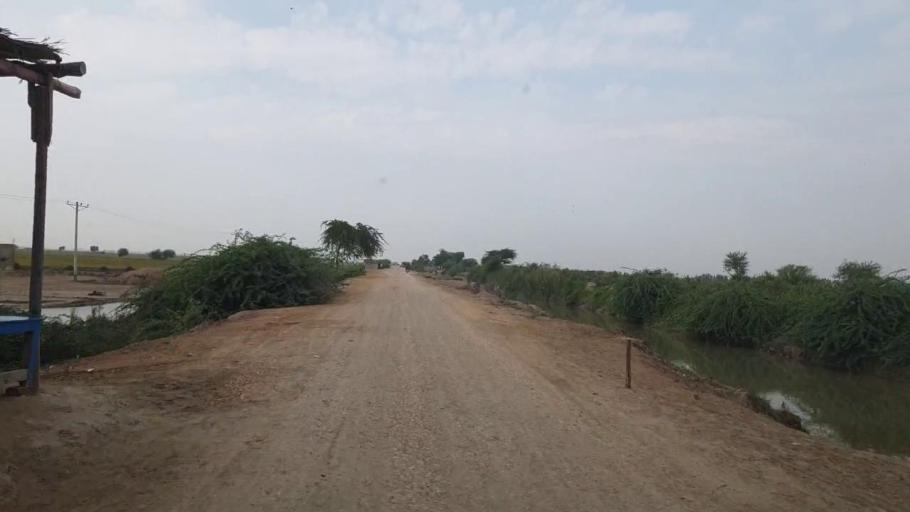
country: PK
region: Sindh
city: Kario
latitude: 24.6079
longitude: 68.5952
